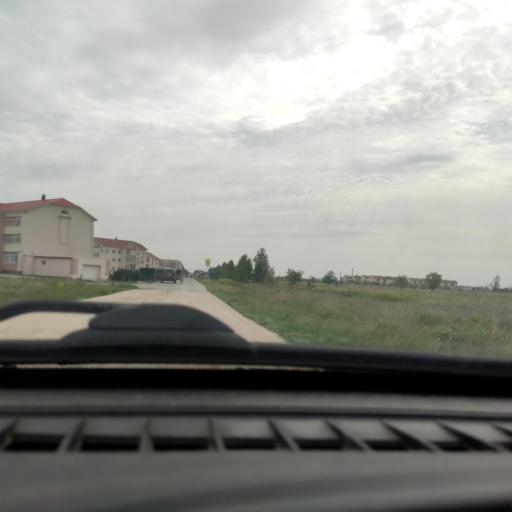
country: RU
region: Samara
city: Podstepki
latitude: 53.5278
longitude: 49.1759
